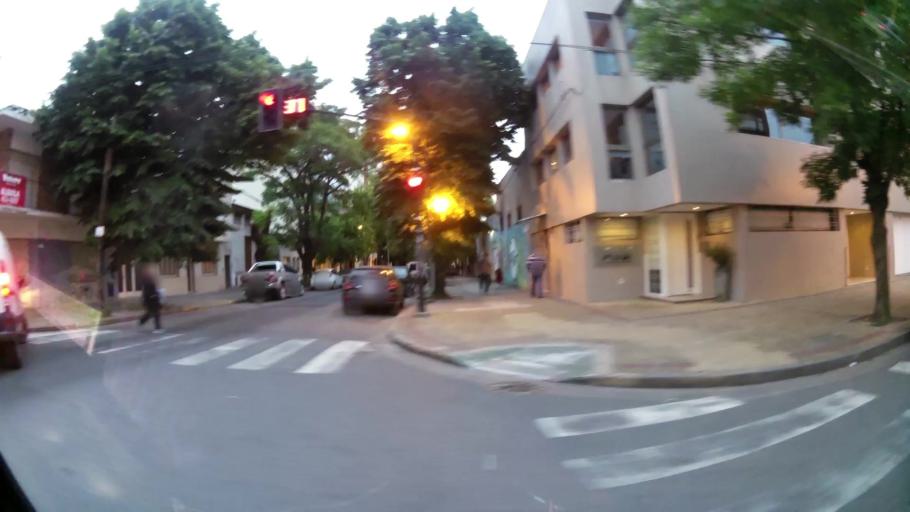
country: AR
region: Buenos Aires
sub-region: Partido de La Plata
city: La Plata
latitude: -34.9181
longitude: -57.9635
